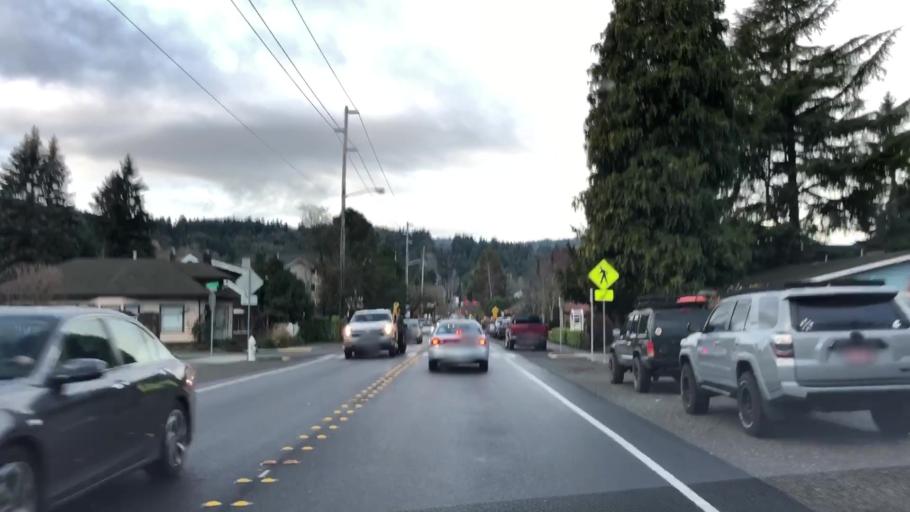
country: US
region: Washington
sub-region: King County
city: Issaquah
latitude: 47.5301
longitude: -122.0296
